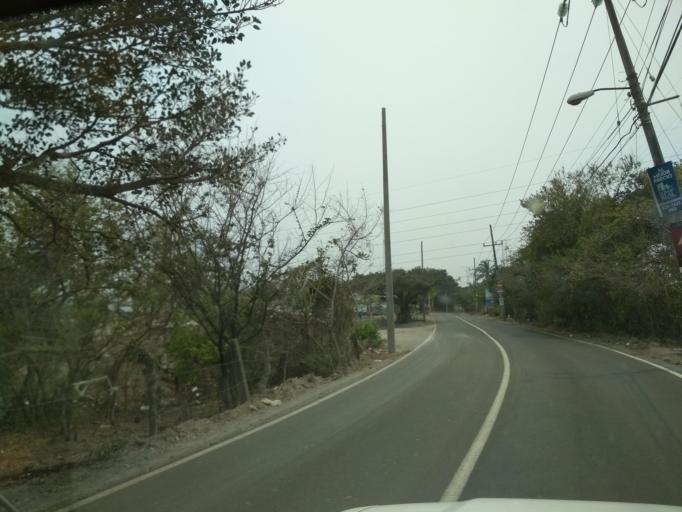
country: MX
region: Veracruz
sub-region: Veracruz
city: Las Amapolas
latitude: 19.1497
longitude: -96.2278
